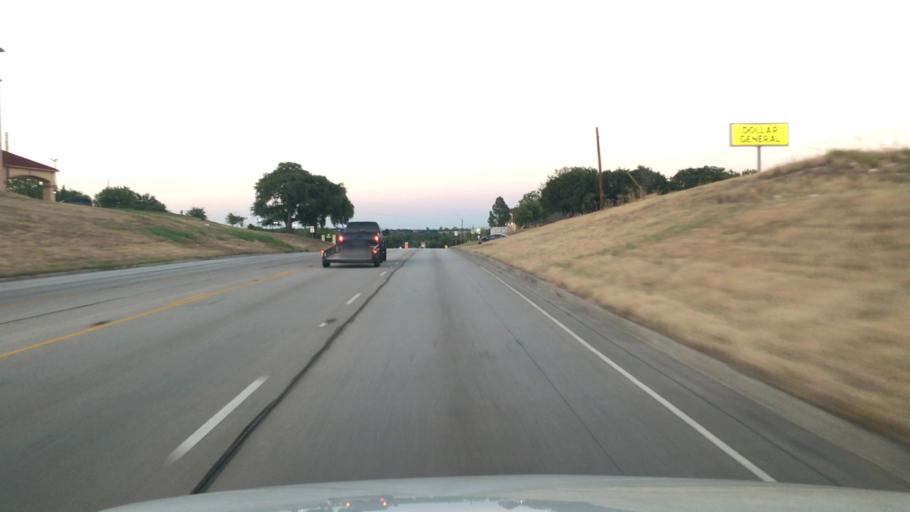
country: US
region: Texas
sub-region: Somervell County
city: Glen Rose
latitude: 32.2373
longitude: -97.7580
